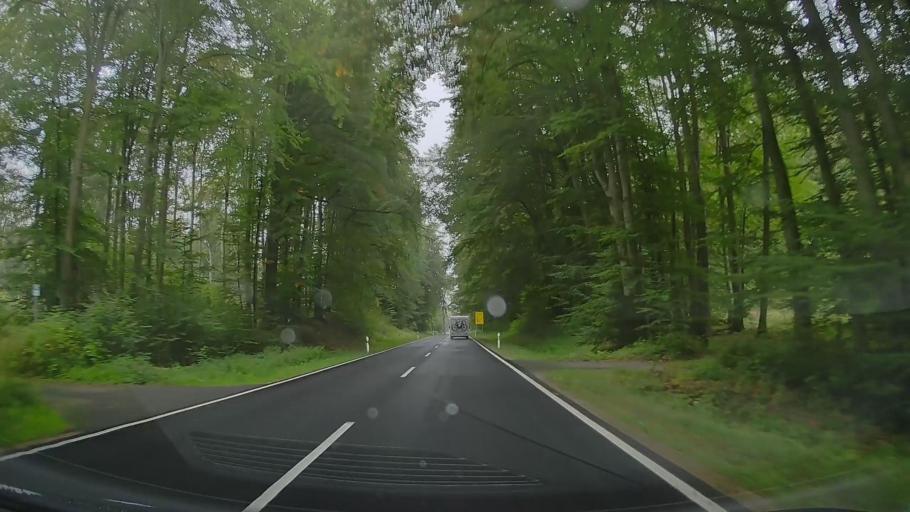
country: DE
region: Mecklenburg-Vorpommern
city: Gaegelow
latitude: 53.7151
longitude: 11.8878
